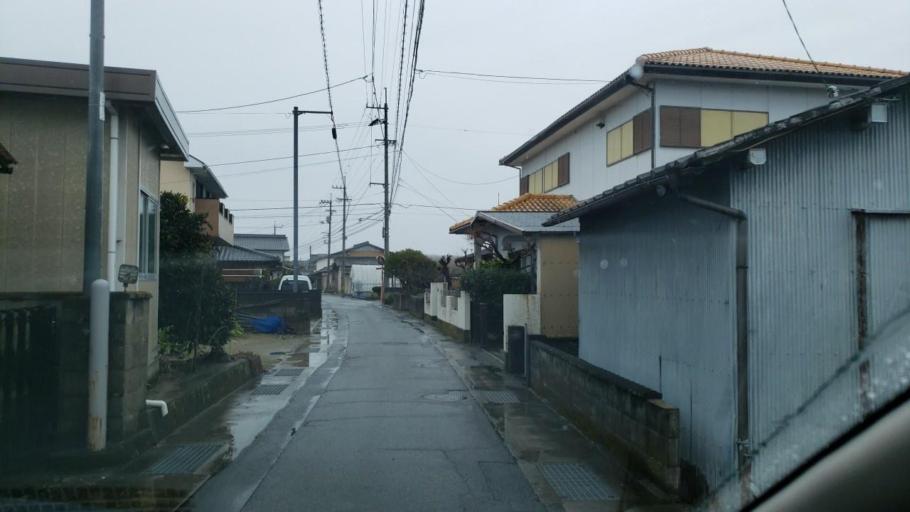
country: JP
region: Tokushima
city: Kamojimacho-jogejima
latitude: 34.0764
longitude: 134.3466
